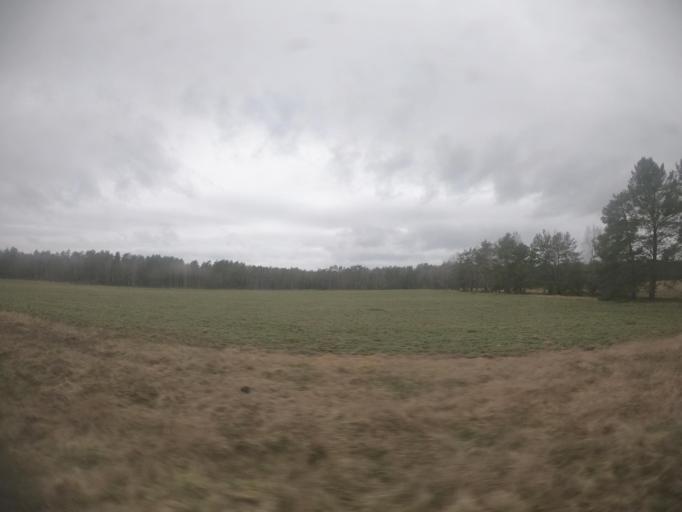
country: PL
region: West Pomeranian Voivodeship
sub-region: Powiat szczecinecki
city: Bialy Bor
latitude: 53.8242
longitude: 16.8712
